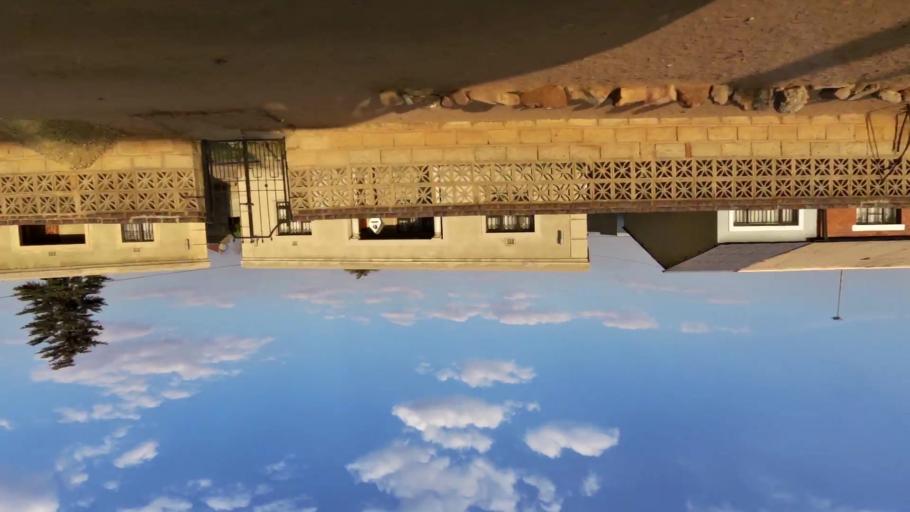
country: ZA
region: Gauteng
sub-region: City of Johannesburg Metropolitan Municipality
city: Soweto
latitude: -26.2338
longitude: 27.9033
